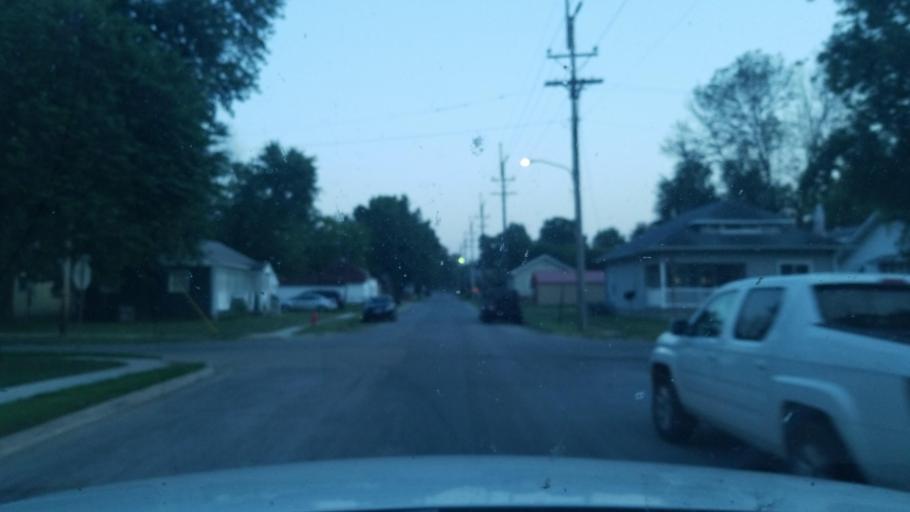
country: US
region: Illinois
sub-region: Saline County
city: Harrisburg
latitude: 37.7305
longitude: -88.5420
